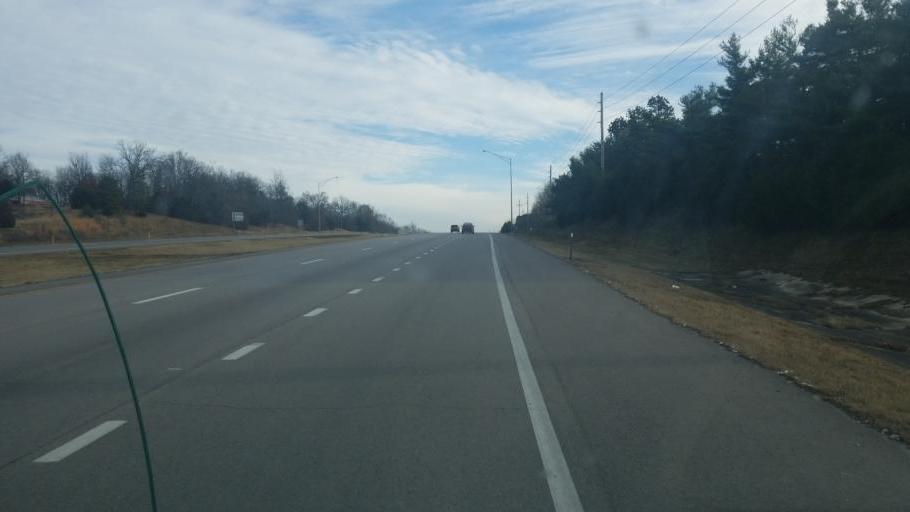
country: US
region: Missouri
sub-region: Stoddard County
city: Dexter
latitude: 36.8101
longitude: -89.9664
